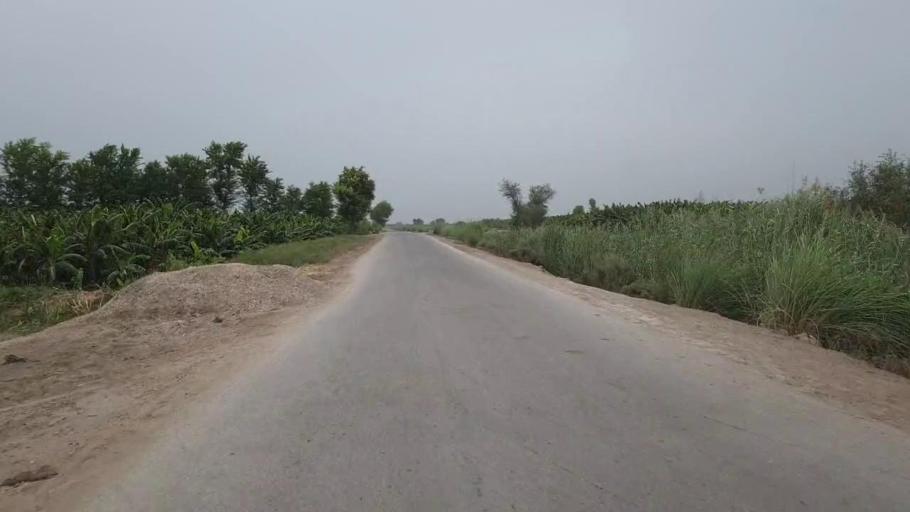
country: PK
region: Sindh
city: Bandhi
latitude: 26.5554
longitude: 68.2091
